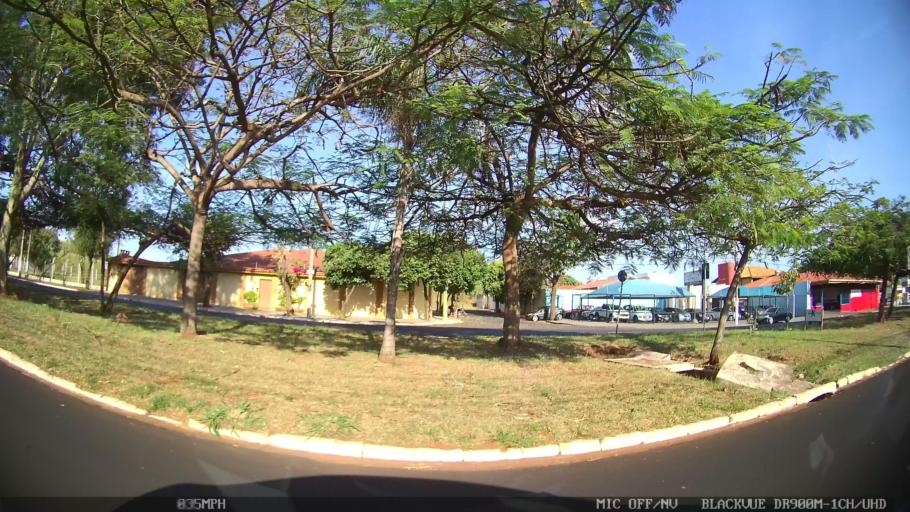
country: BR
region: Sao Paulo
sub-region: Ribeirao Preto
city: Ribeirao Preto
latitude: -21.2103
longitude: -47.7721
